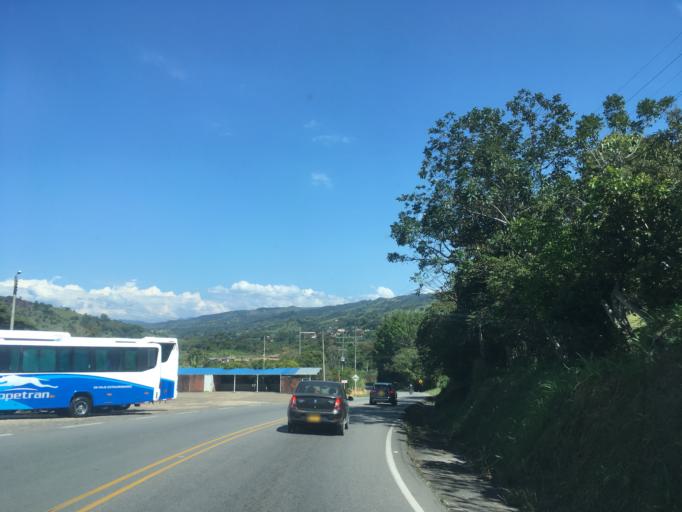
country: CO
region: Santander
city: Suaita
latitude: 6.0664
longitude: -73.4254
